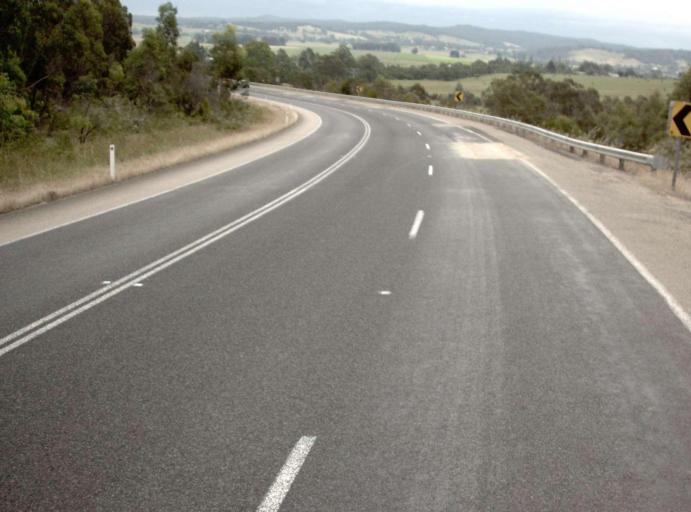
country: AU
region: Victoria
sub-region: East Gippsland
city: Lakes Entrance
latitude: -37.7205
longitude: 147.8540
